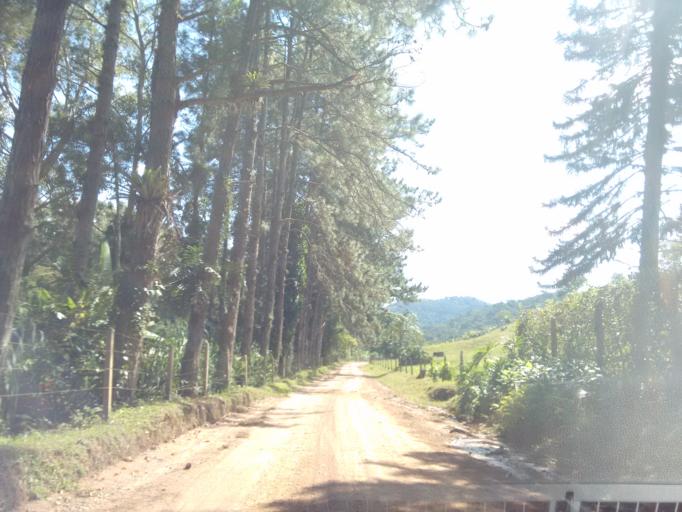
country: BR
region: Santa Catarina
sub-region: Indaial
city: Indaial
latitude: -26.9236
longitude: -49.1868
